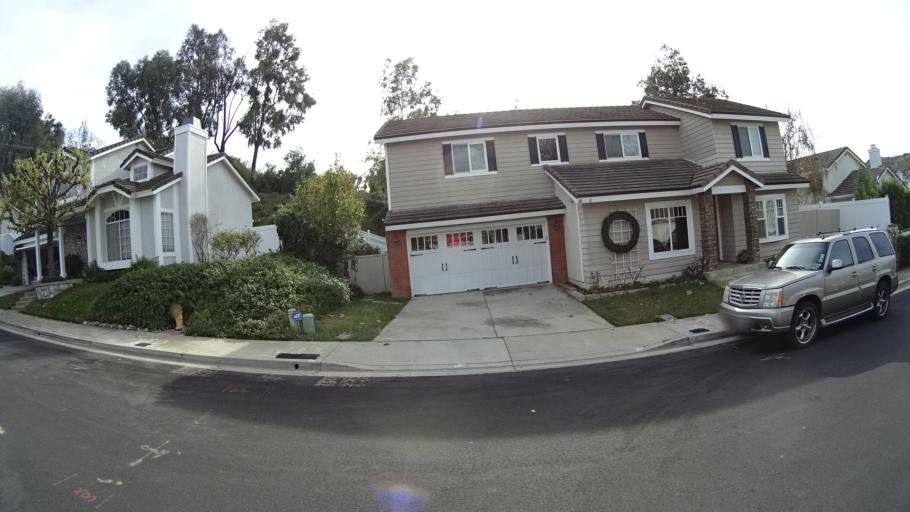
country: US
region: California
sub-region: Orange County
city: Laguna Woods
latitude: 33.5969
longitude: -117.7457
